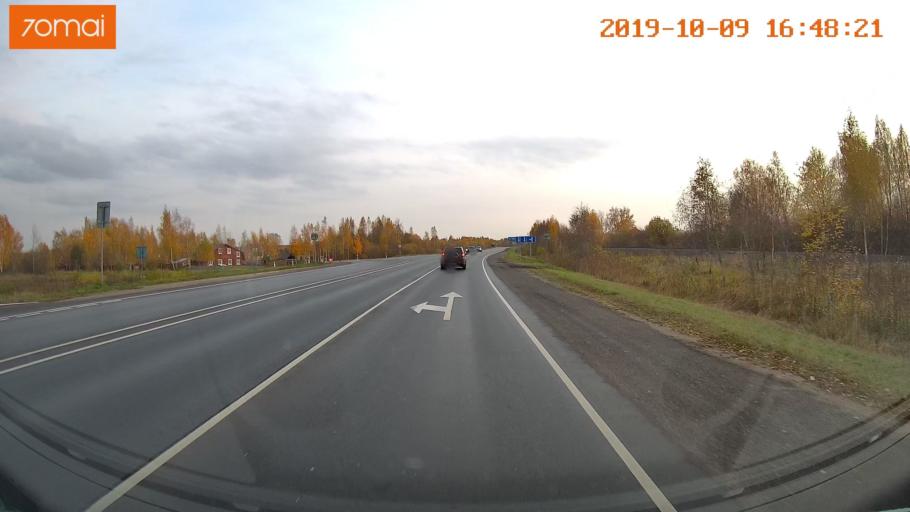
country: RU
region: Kostroma
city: Volgorechensk
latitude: 57.4283
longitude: 41.1901
